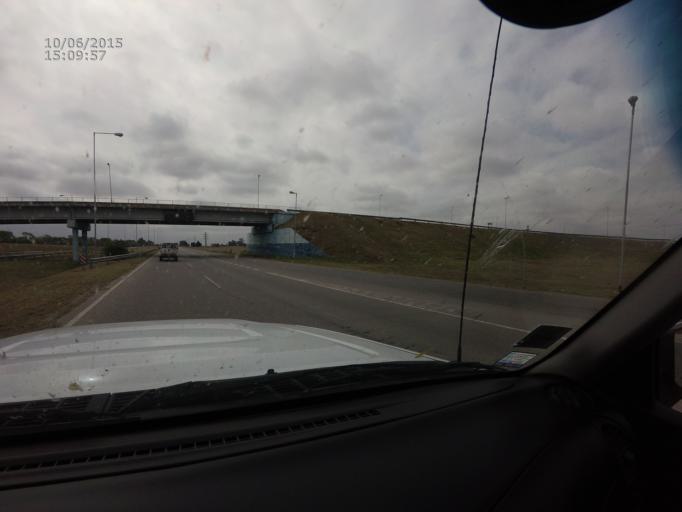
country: AR
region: Cordoba
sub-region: Departamento de Rio Segundo
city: Rio Segundo
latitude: -31.6288
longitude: -63.8766
